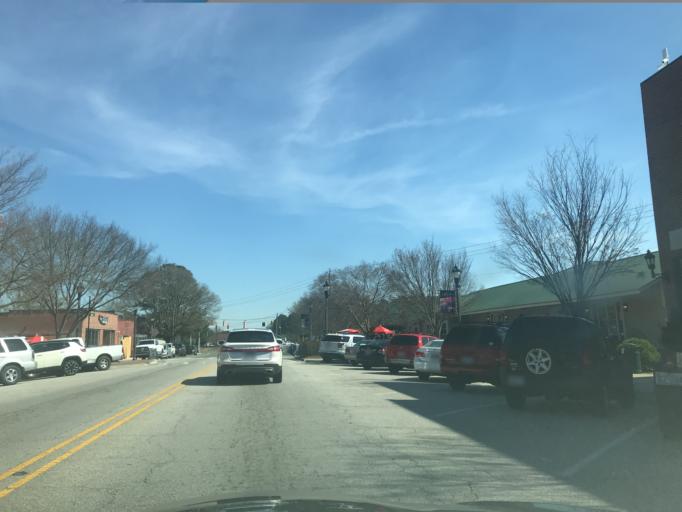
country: US
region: North Carolina
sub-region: Wake County
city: Fuquay-Varina
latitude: 35.5932
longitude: -78.7942
